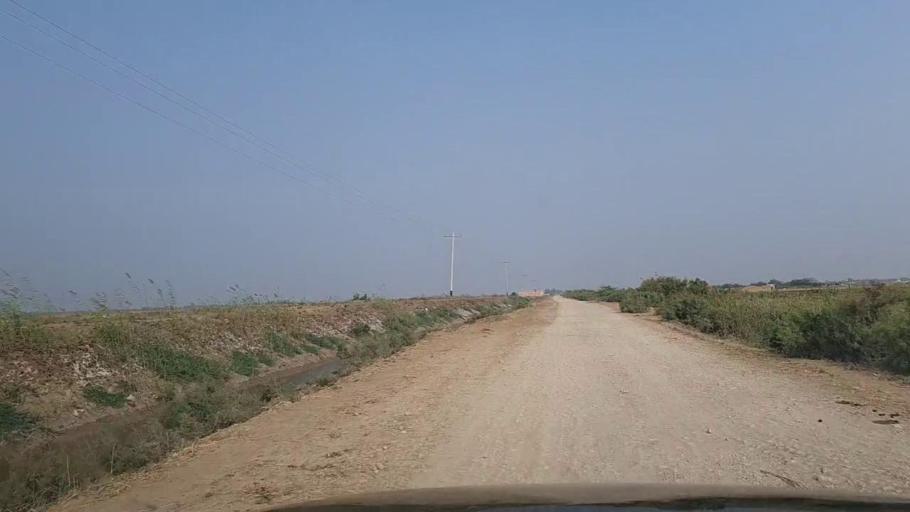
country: PK
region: Sindh
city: Thatta
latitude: 24.7543
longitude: 67.8721
